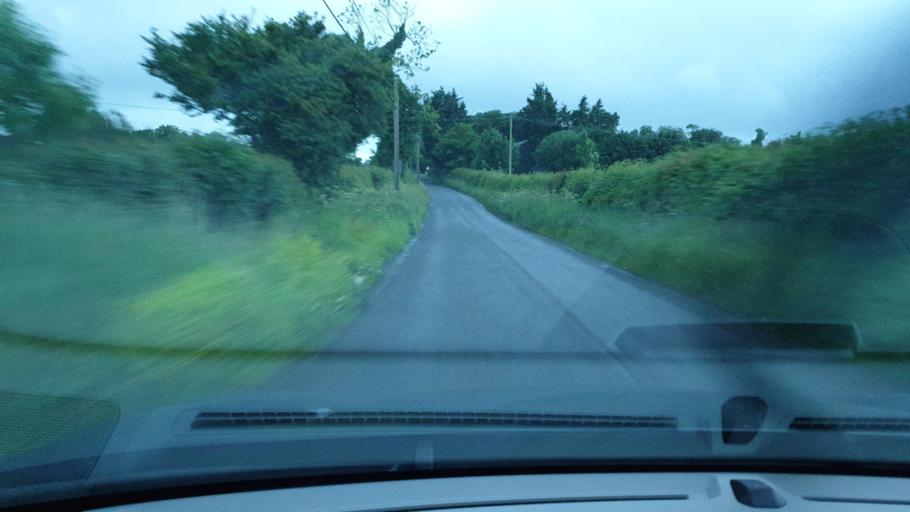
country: IE
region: Leinster
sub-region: An Mhi
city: Ashbourne
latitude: 53.5260
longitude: -6.3404
